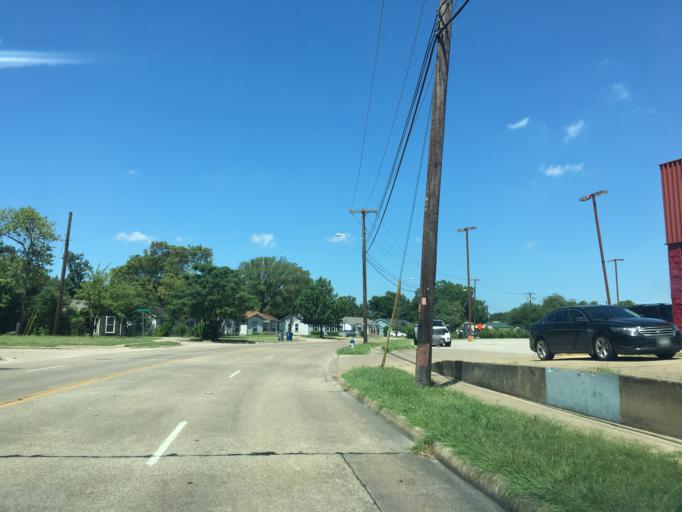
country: US
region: Texas
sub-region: Dallas County
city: Garland
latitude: 32.8431
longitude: -96.6869
